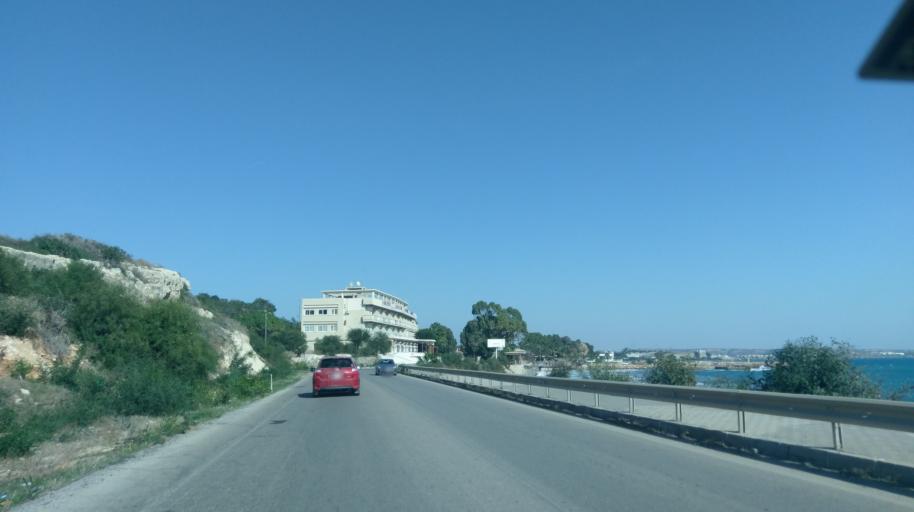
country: CY
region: Ammochostos
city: Trikomo
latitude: 35.3104
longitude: 33.9498
